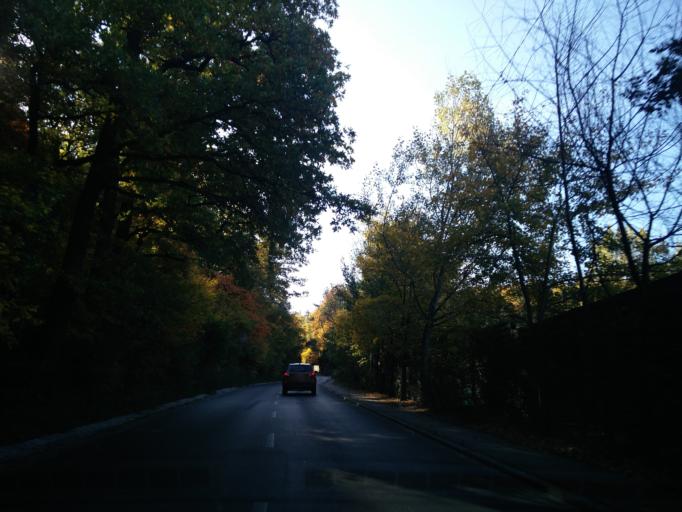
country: HU
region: Pest
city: Budakeszi
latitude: 47.5319
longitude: 18.9472
